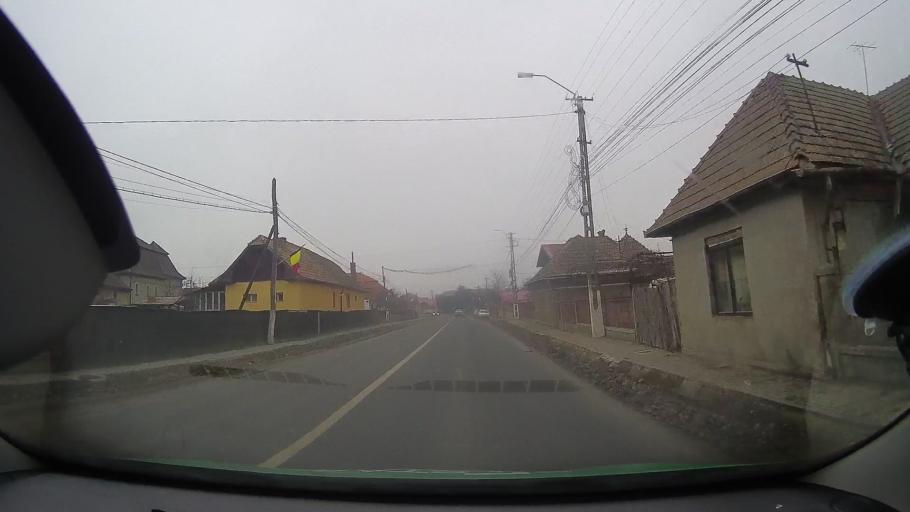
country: RO
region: Cluj
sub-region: Comuna Mihai Viteazu
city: Mihai Viteazu
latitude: 46.5408
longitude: 23.7554
